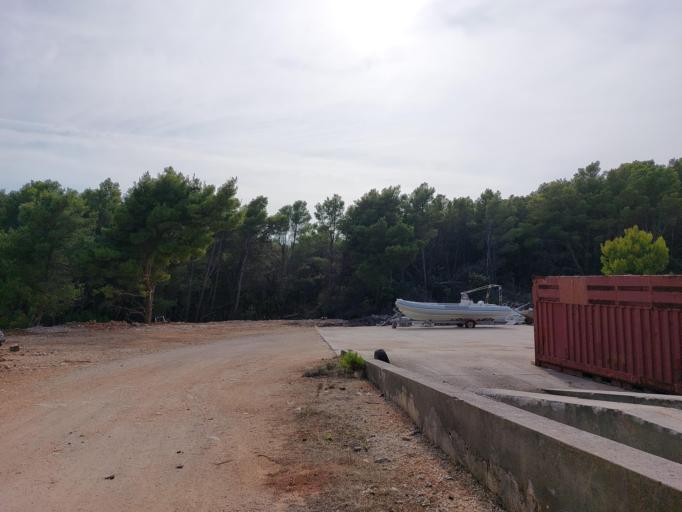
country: HR
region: Dubrovacko-Neretvanska
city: Smokvica
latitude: 42.7370
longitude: 16.8316
